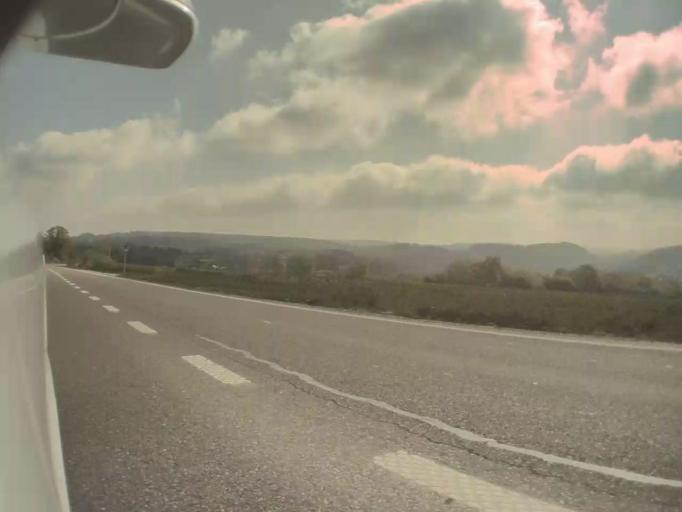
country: BE
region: Wallonia
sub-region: Province du Luxembourg
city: Marche-en-Famenne
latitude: 50.1875
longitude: 5.2958
